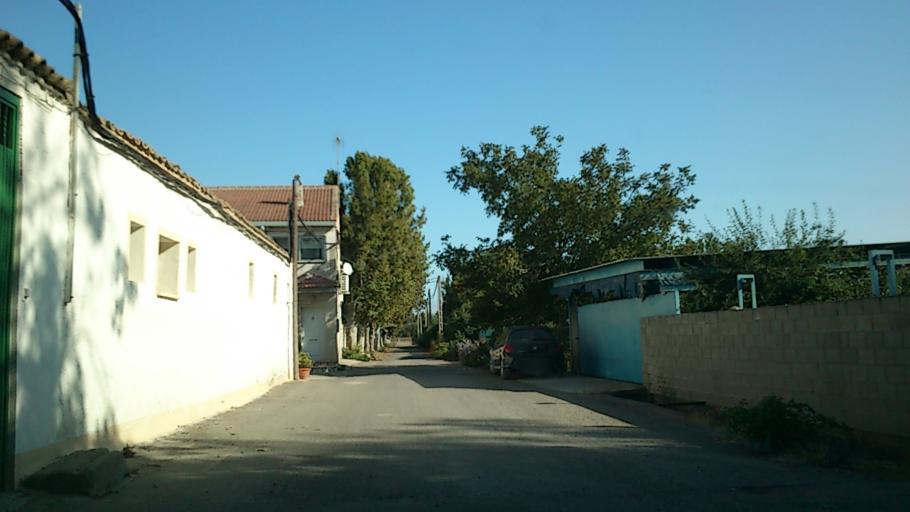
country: ES
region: Aragon
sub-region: Provincia de Zaragoza
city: Villanueva de Gallego
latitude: 41.7296
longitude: -0.7968
